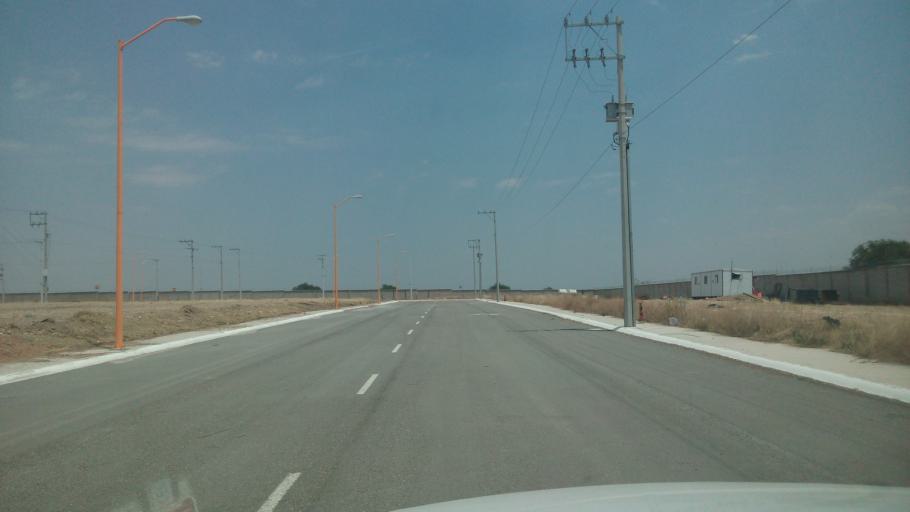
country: MX
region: Aguascalientes
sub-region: Aguascalientes
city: Villa Licenciado Jesus Teran (Calvillito)
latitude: 21.8669
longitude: -102.1758
